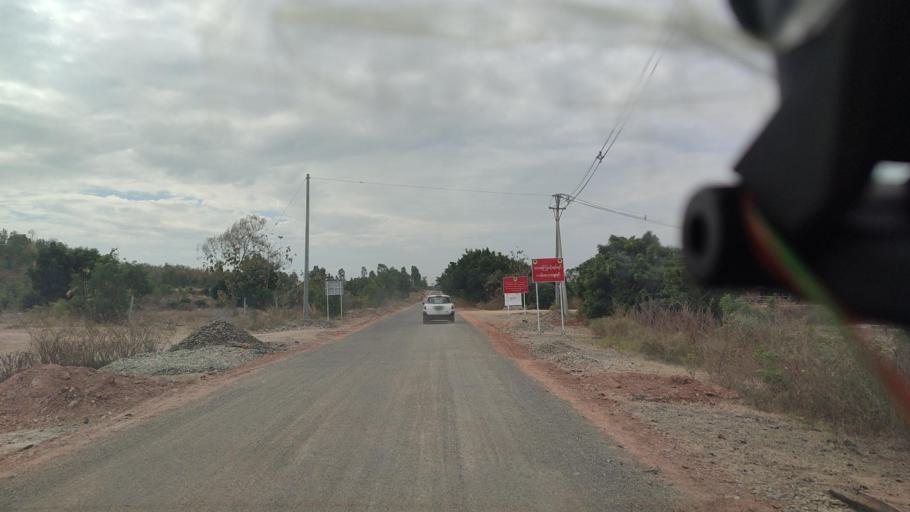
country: MM
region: Mandalay
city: Pyinmana
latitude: 19.7531
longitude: 96.3219
